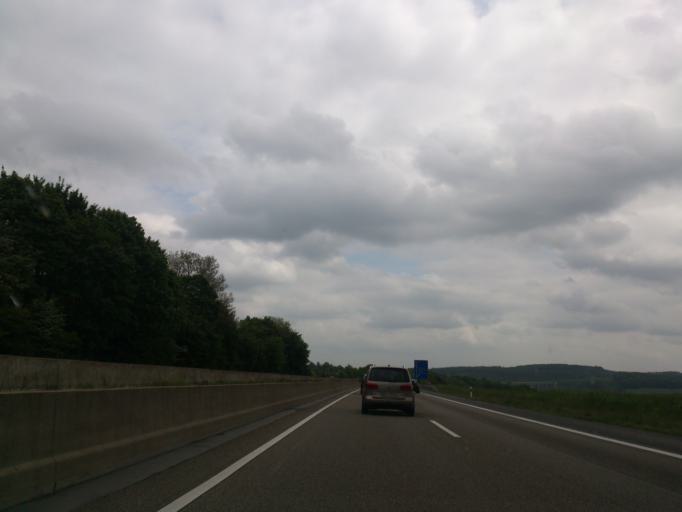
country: DE
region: North Rhine-Westphalia
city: Warburg
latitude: 51.4742
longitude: 9.0935
